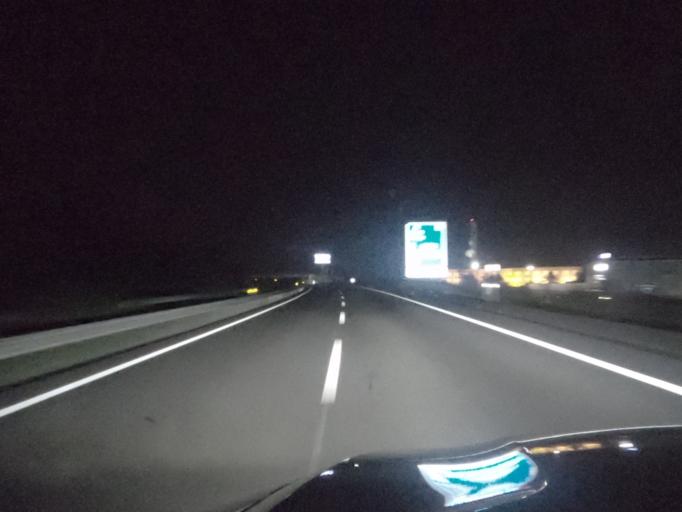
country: PT
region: Aveiro
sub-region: Mealhada
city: Mealhada
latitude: 40.3614
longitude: -8.4924
